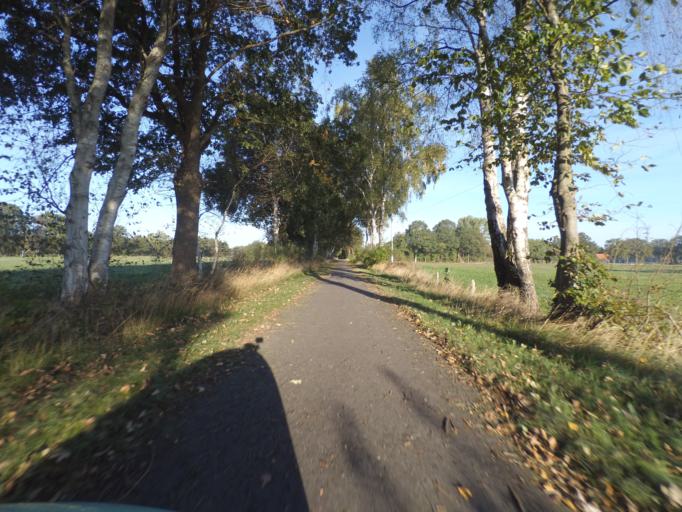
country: NL
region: Gelderland
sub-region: Gemeente Winterswijk
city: Winterswijk
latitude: 52.0004
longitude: 6.6620
